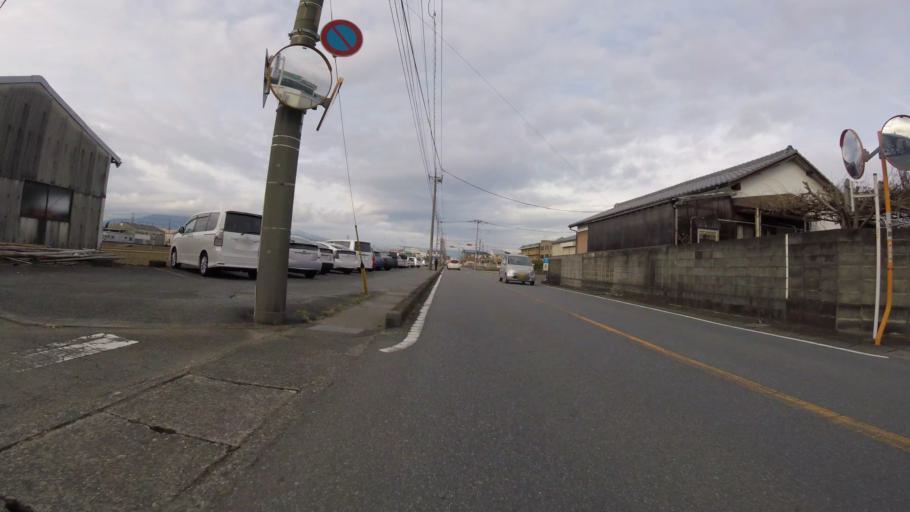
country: JP
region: Shizuoka
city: Mishima
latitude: 35.0960
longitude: 138.9117
